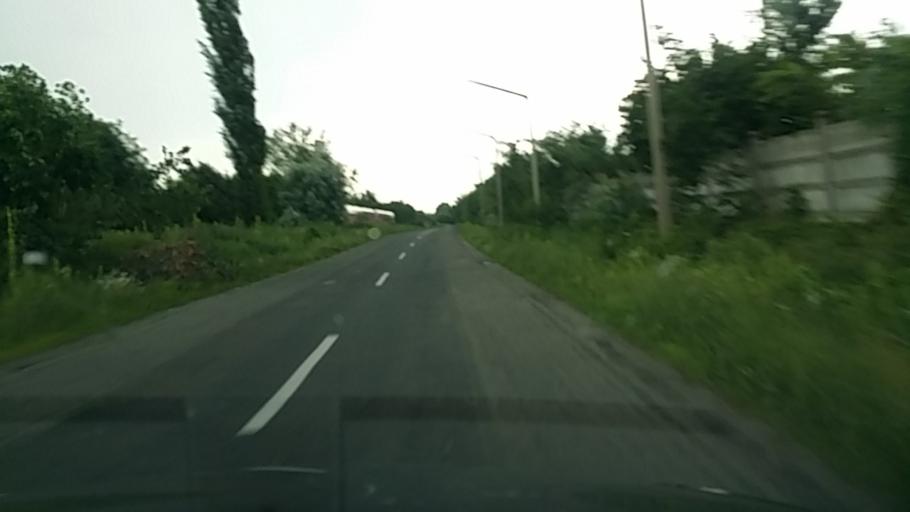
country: HU
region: Pest
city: Ocsa
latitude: 47.2843
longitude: 19.2670
